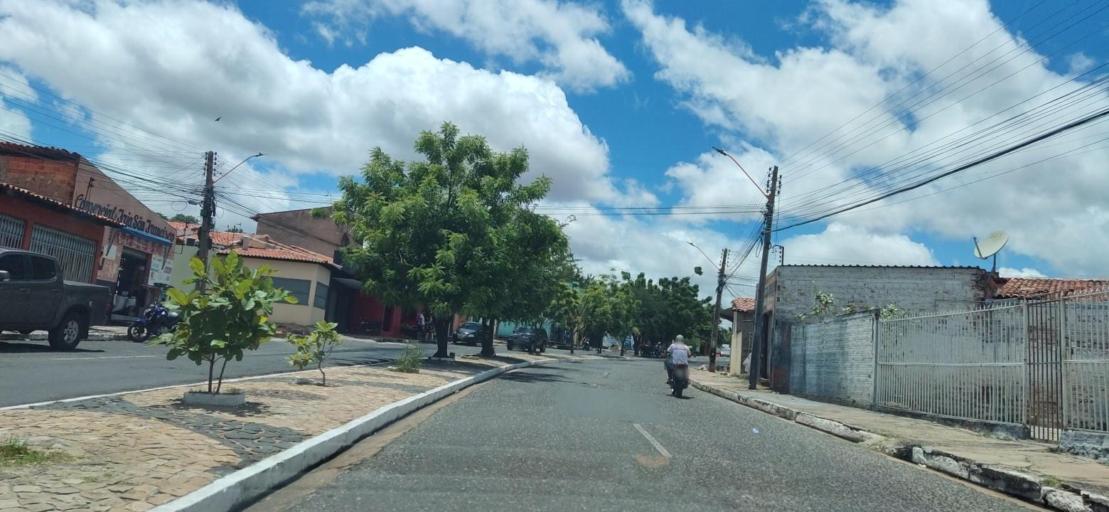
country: BR
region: Piaui
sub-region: Teresina
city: Teresina
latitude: -5.1458
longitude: -42.7795
